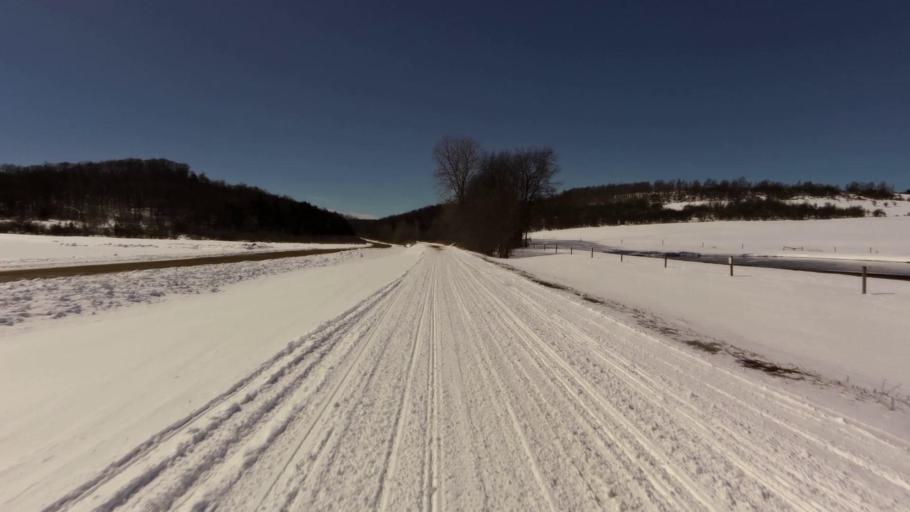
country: US
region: New York
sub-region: Cattaraugus County
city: Delevan
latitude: 42.4387
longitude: -78.4322
